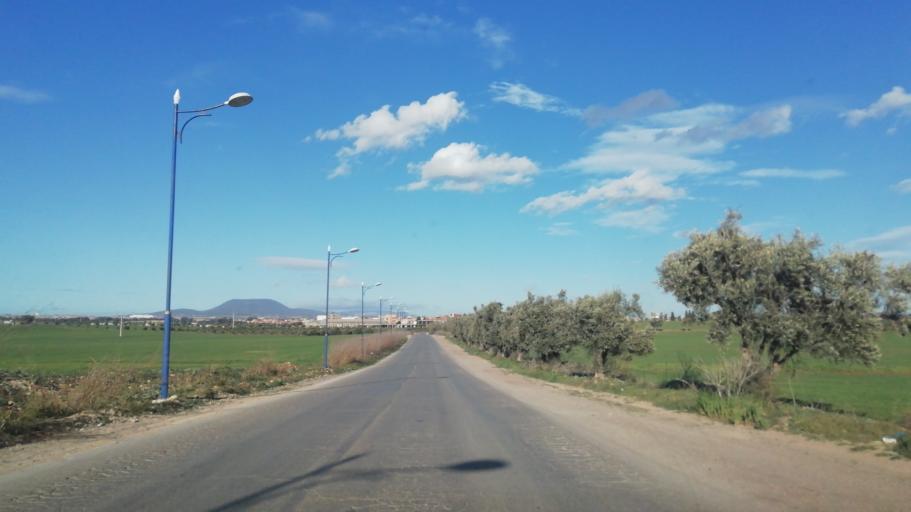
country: DZ
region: Oran
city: Sidi ech Chahmi
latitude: 35.6492
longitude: -0.5315
